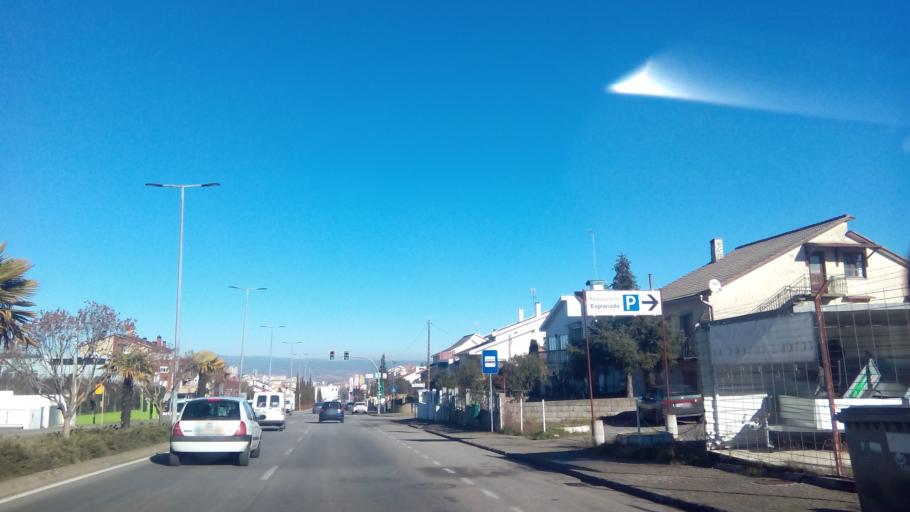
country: PT
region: Braganca
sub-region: Braganca Municipality
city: Braganca
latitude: 41.7846
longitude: -6.7761
